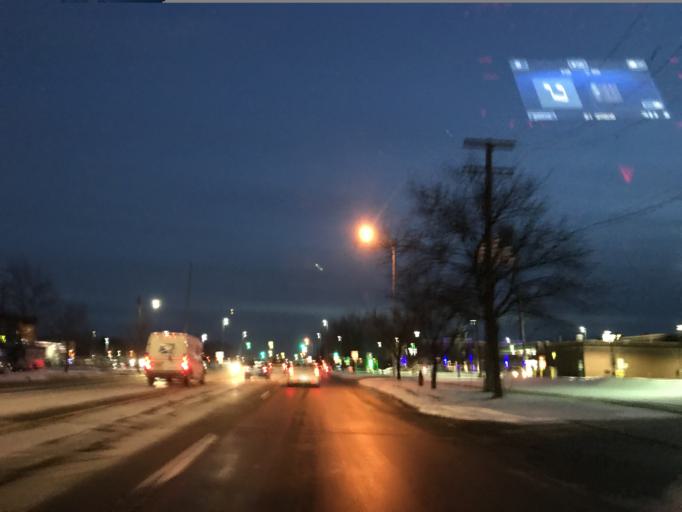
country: US
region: Michigan
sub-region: Wayne County
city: Redford
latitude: 42.3858
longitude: -83.3144
